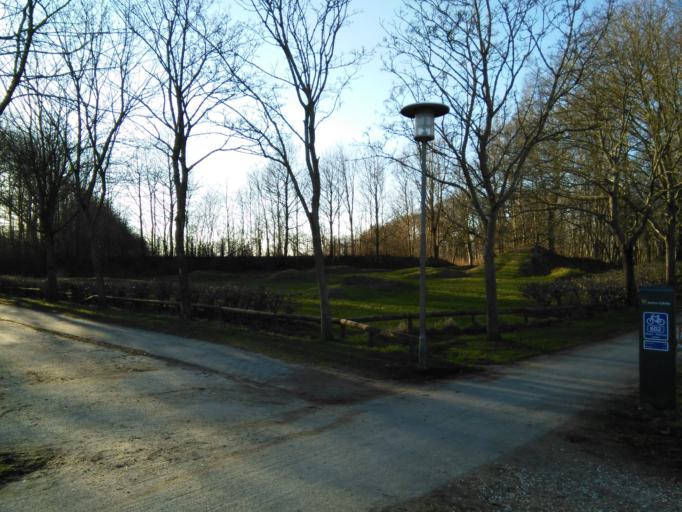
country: DK
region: Central Jutland
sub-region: Arhus Kommune
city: Malling
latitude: 56.0460
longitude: 10.1995
